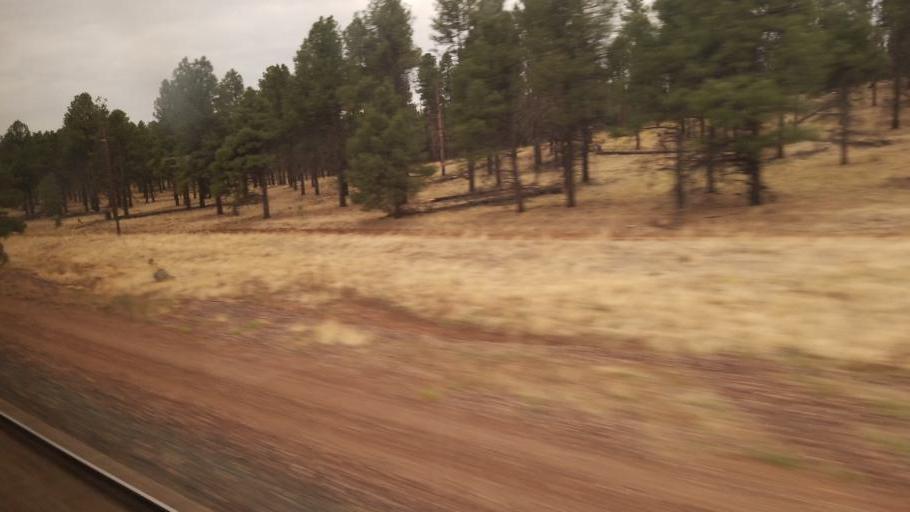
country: US
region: Arizona
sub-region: Coconino County
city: Parks
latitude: 35.2444
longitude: -112.0348
